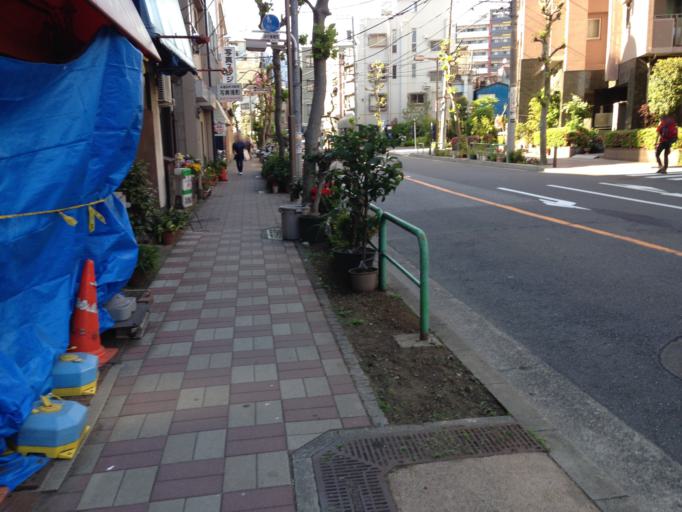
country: JP
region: Tokyo
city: Urayasu
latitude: 35.6882
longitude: 139.7940
